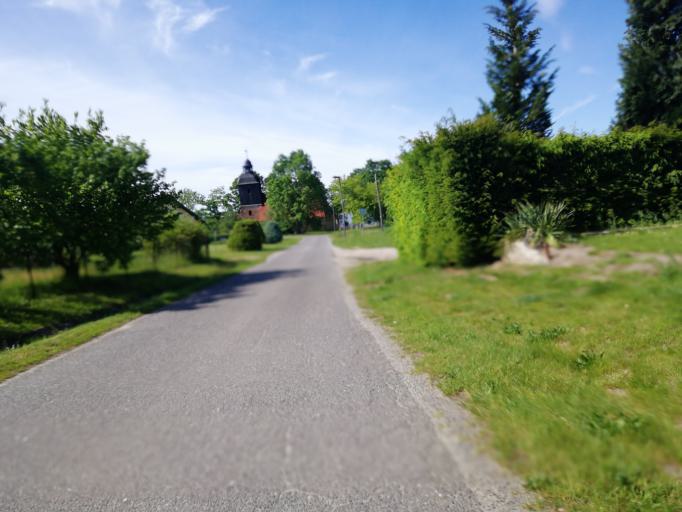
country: DE
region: Brandenburg
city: Calau
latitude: 51.7318
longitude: 13.9122
